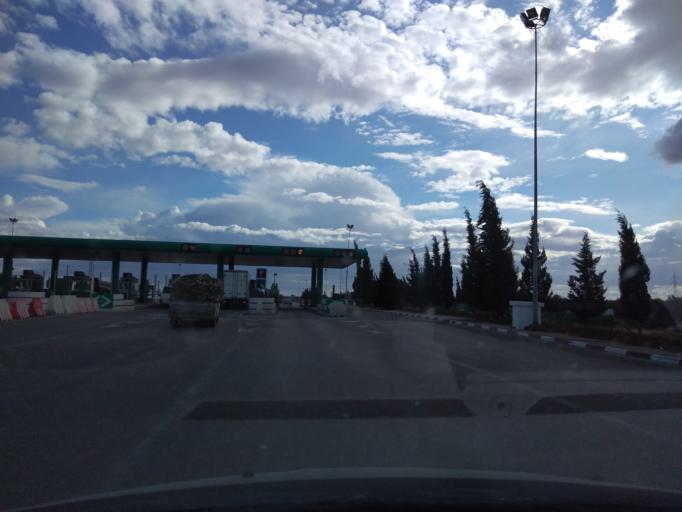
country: TN
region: Susah
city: Masakin
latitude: 35.6909
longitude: 10.5633
